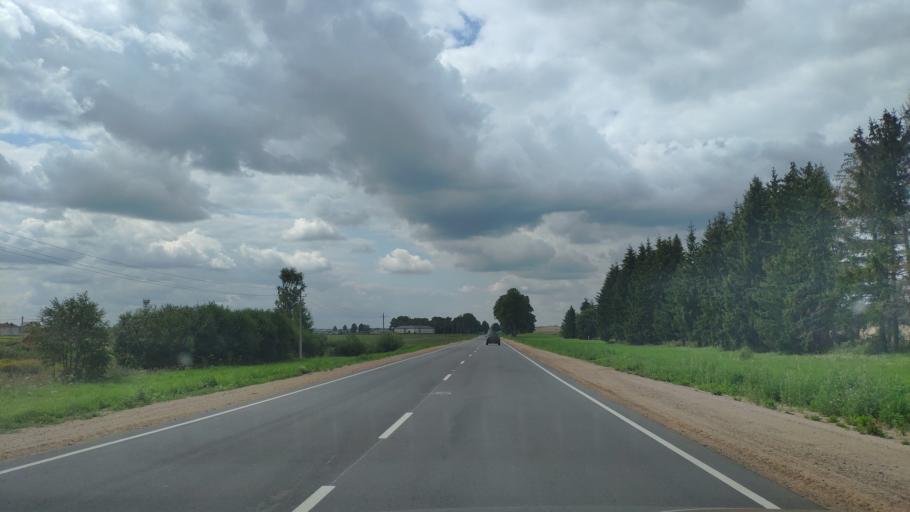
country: BY
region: Minsk
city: Zaslawye
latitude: 54.0054
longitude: 27.3465
